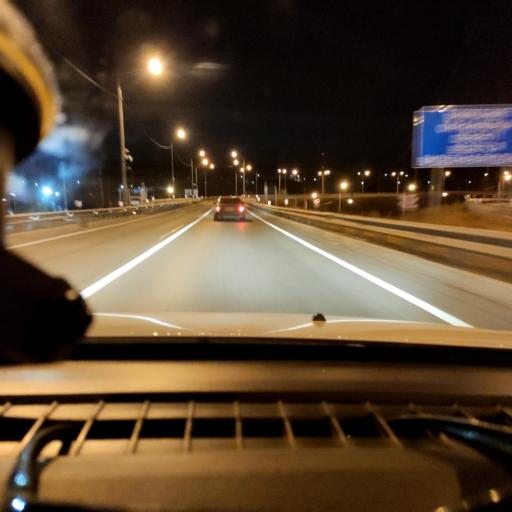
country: RU
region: Samara
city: Volzhskiy
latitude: 53.4341
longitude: 50.1164
